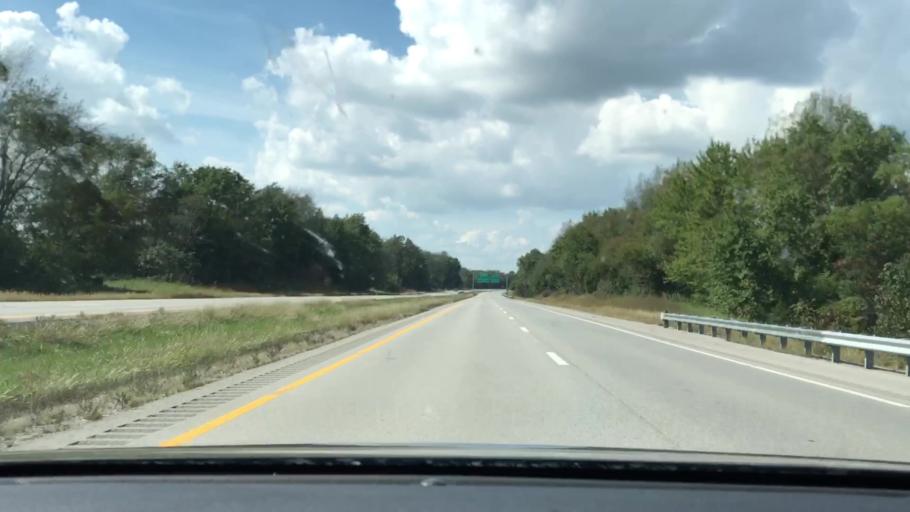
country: US
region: Kentucky
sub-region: Barren County
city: Cave City
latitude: 37.0494
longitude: -86.0900
